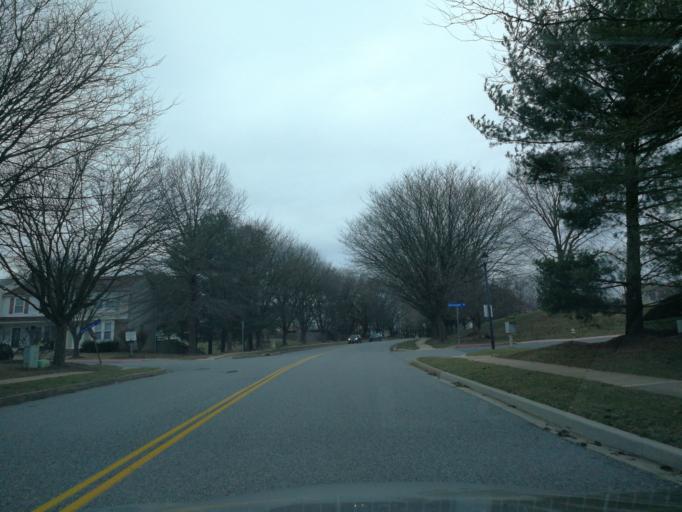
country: US
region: Maryland
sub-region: Harford County
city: Bel Air South
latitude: 39.4712
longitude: -76.3197
